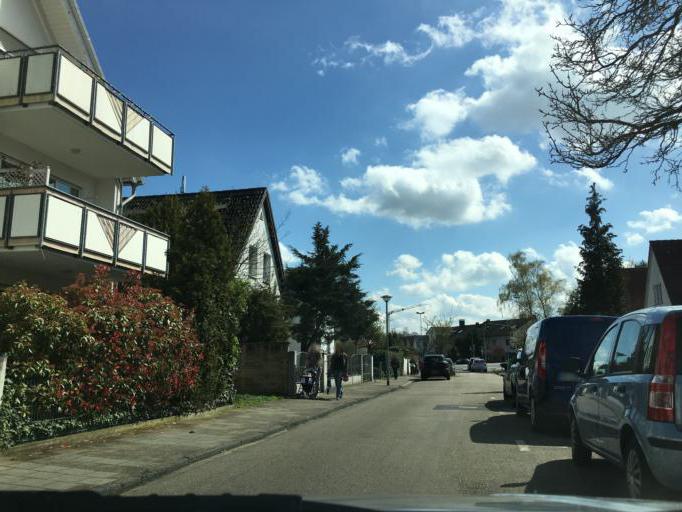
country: DE
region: Hesse
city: Heusenstamm
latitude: 50.0549
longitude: 8.8058
